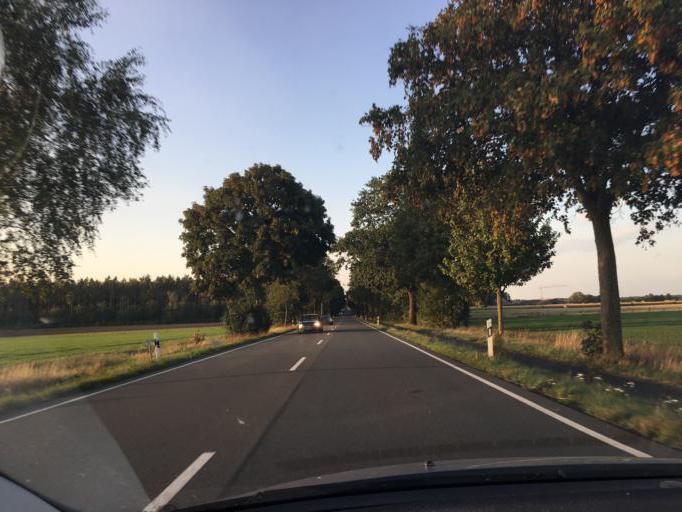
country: DE
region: Lower Saxony
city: Wietzendorf
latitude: 52.8817
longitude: 9.9157
